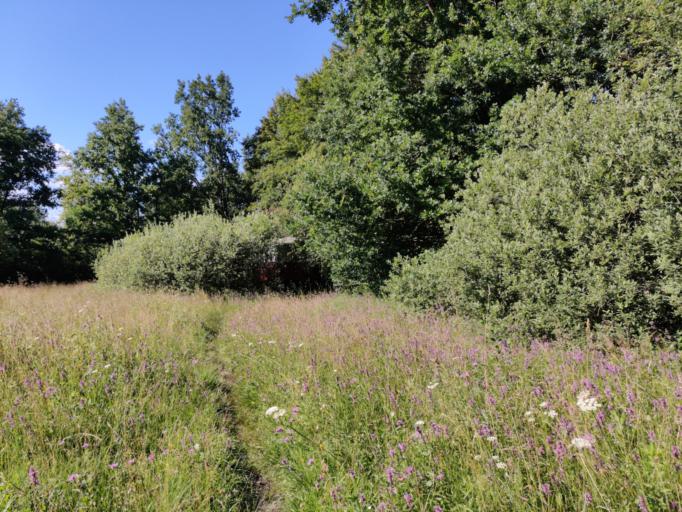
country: AT
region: Carinthia
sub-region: Klagenfurt am Woerthersee
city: Klagenfurt am Woerthersee
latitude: 46.6127
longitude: 14.2571
